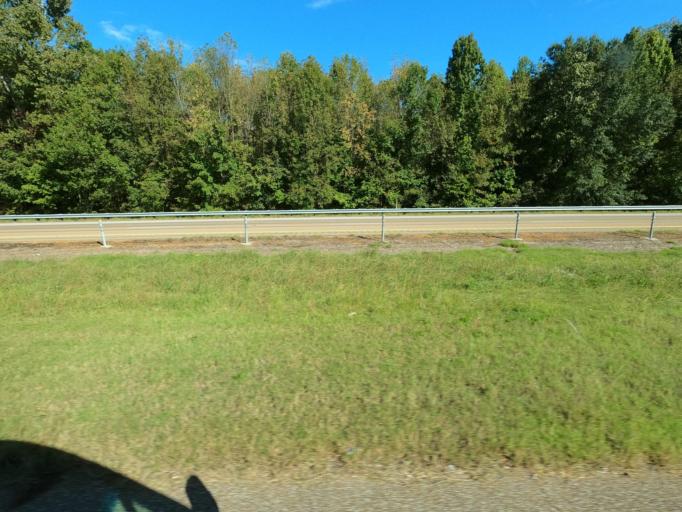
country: US
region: Tennessee
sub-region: Shelby County
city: Millington
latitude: 35.3096
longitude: -89.8492
